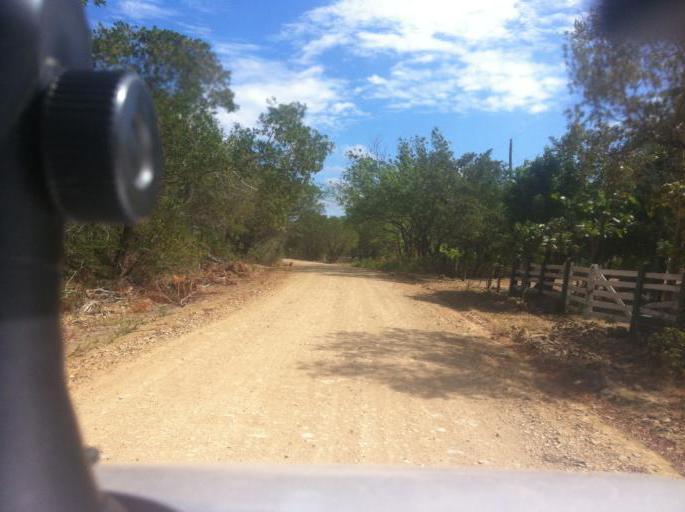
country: NI
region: Rivas
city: Tola
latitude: 11.4768
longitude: -86.1067
